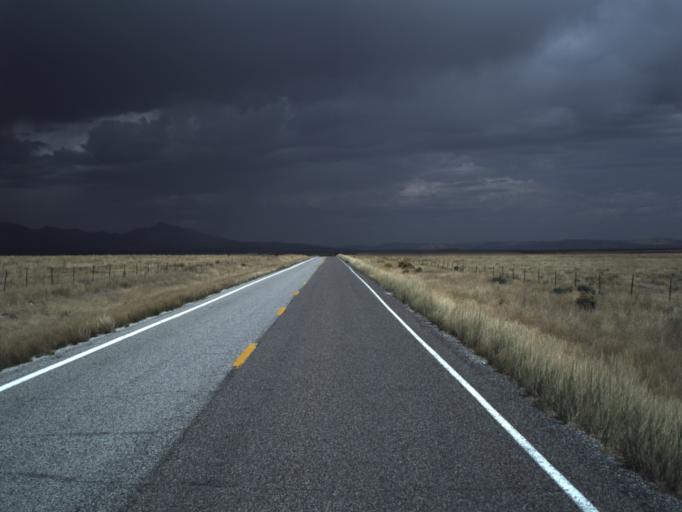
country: US
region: Idaho
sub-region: Oneida County
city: Malad City
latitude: 41.8805
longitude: -113.1176
